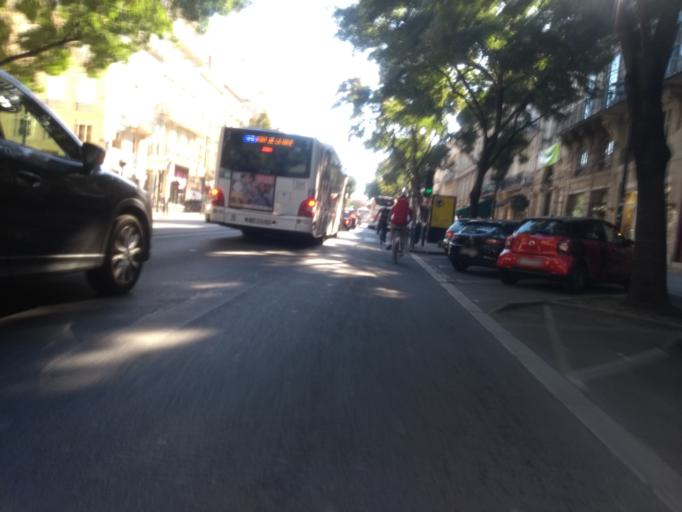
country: FR
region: Aquitaine
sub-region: Departement de la Gironde
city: Bordeaux
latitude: 44.8440
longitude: -0.5788
